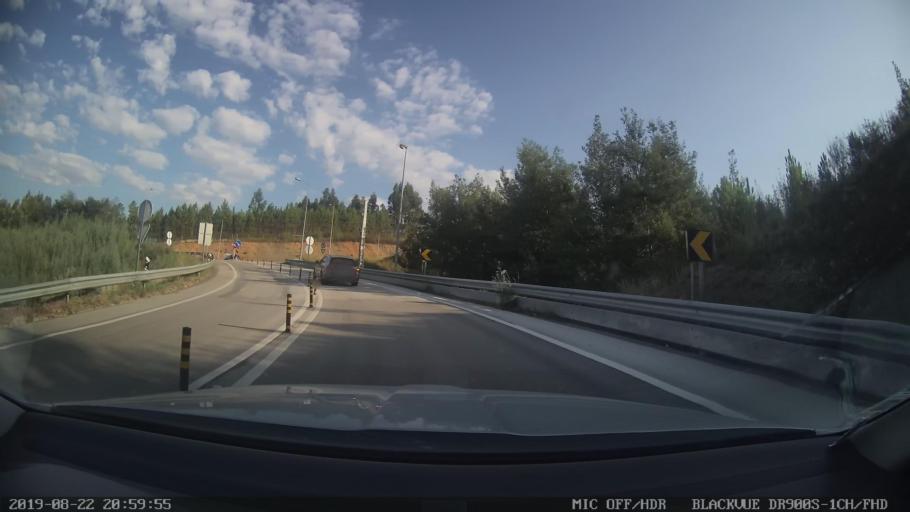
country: PT
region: Castelo Branco
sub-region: Serta
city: Serta
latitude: 39.8153
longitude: -8.0901
